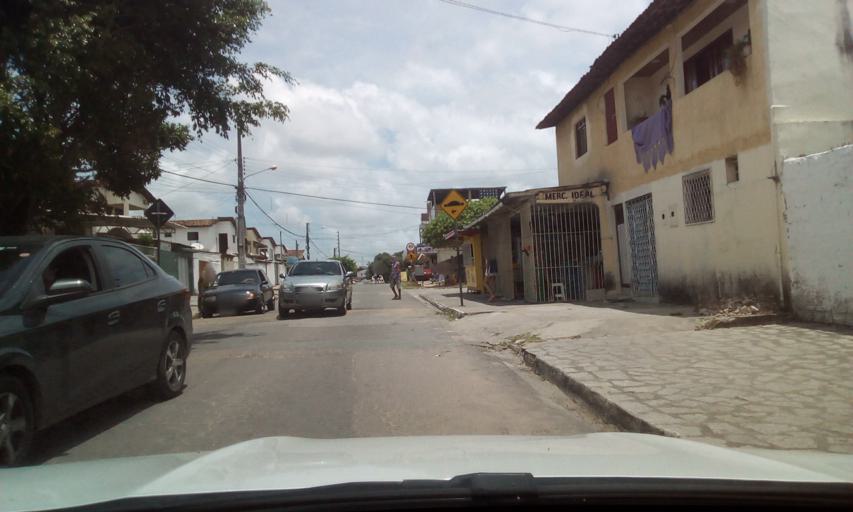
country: BR
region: Paraiba
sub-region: Joao Pessoa
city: Joao Pessoa
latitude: -7.1705
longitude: -34.8876
